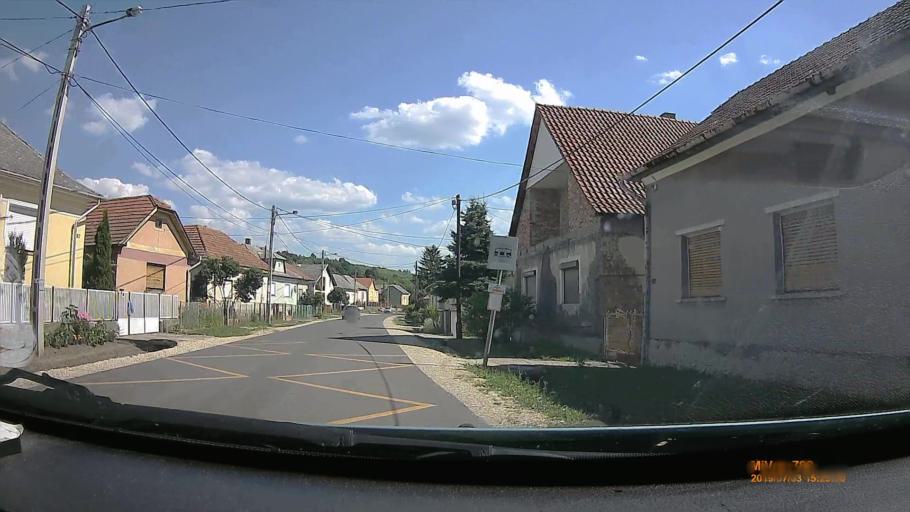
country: HU
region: Borsod-Abauj-Zemplen
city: Farkaslyuk
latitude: 48.1899
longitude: 20.3948
